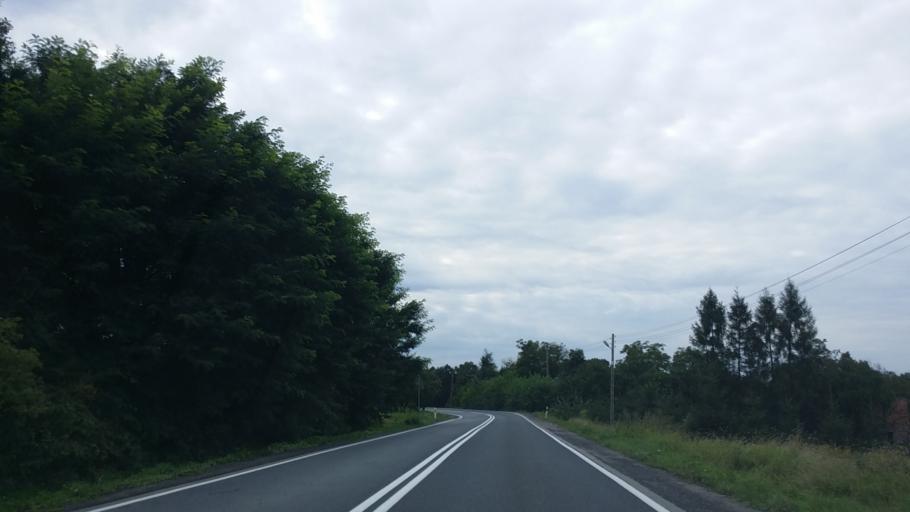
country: PL
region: Lesser Poland Voivodeship
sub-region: Powiat wadowicki
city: Laczany
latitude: 49.9672
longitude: 19.5954
